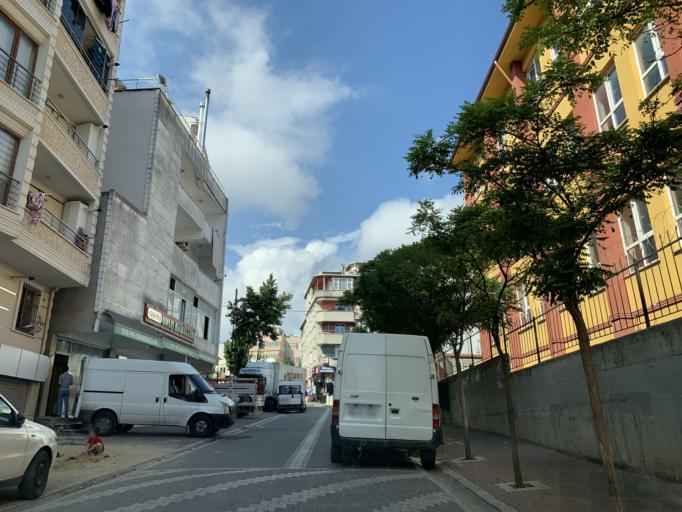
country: TR
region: Istanbul
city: Esenyurt
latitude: 41.0359
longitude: 28.6717
